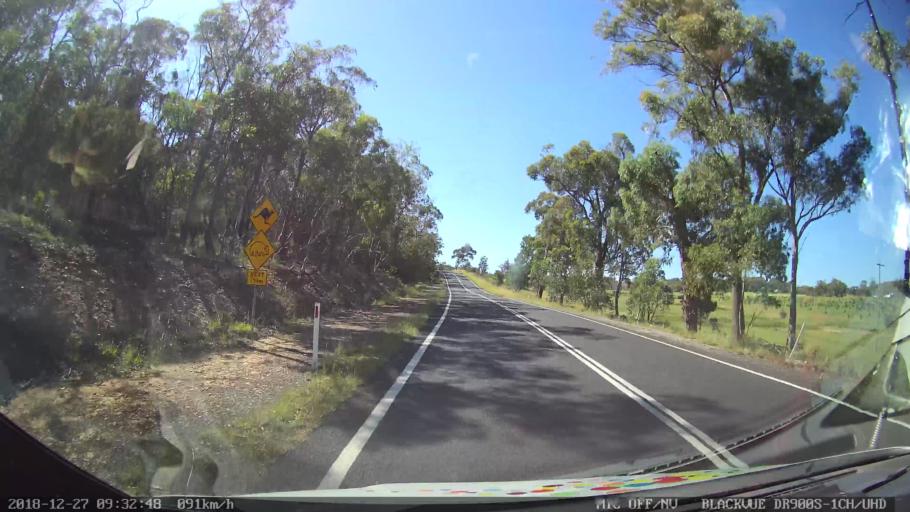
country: AU
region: New South Wales
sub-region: Lithgow
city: Portland
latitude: -33.2119
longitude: 150.0176
